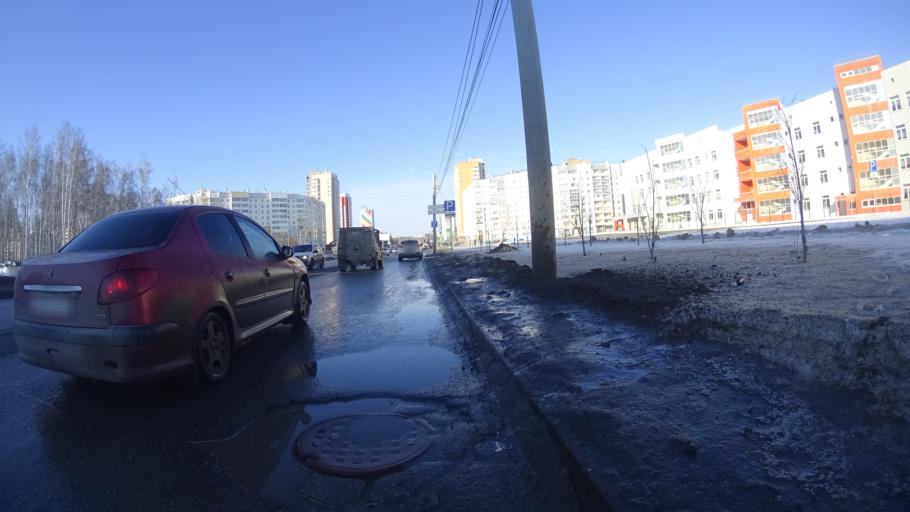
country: RU
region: Chelyabinsk
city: Roshchino
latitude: 55.2057
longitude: 61.2844
